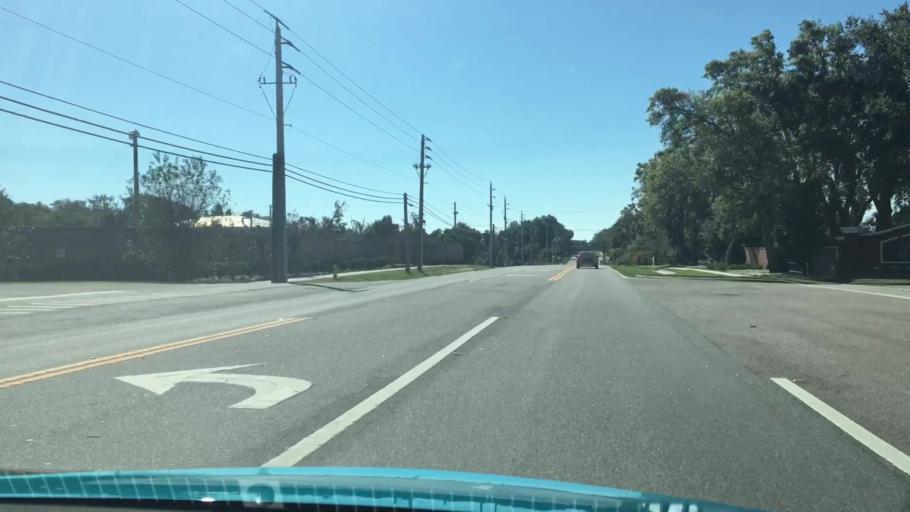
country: US
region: Florida
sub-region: Seminole County
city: Heathrow
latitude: 28.7966
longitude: -81.3630
